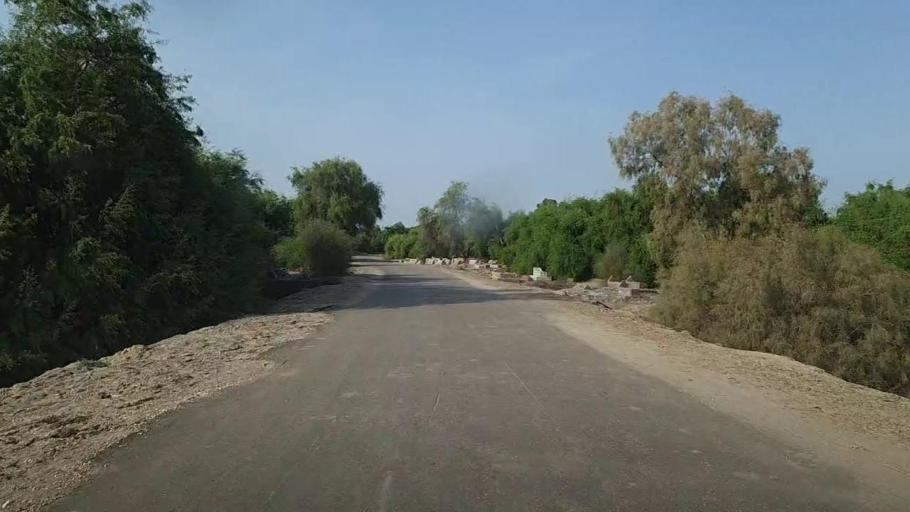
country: PK
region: Sindh
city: Ubauro
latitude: 28.1131
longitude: 69.8511
